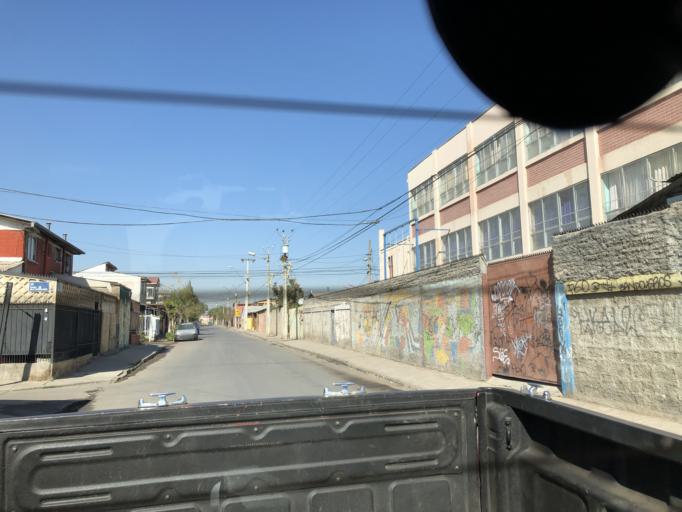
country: CL
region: Santiago Metropolitan
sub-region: Provincia de Cordillera
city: Puente Alto
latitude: -33.5649
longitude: -70.5663
